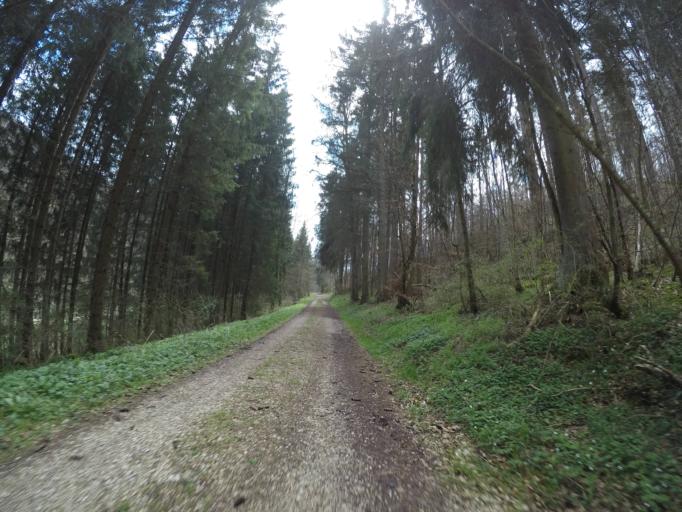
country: DE
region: Baden-Wuerttemberg
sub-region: Tuebingen Region
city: Berghulen
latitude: 48.4916
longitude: 9.7979
